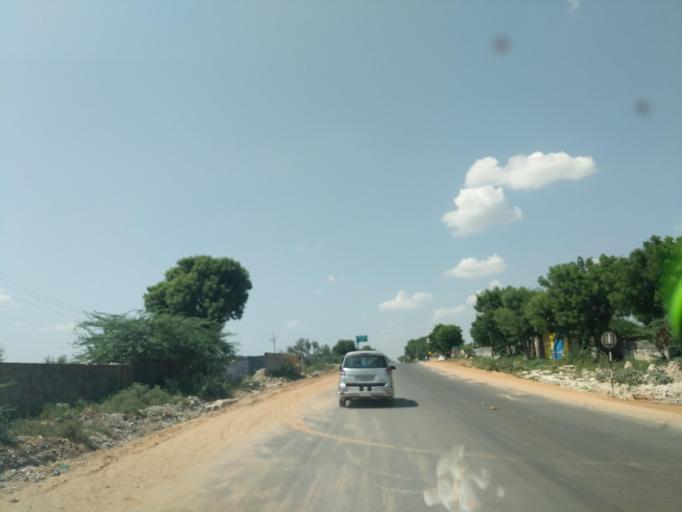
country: IN
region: Rajasthan
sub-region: Nagaur
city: Makrana
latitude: 27.0237
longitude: 74.7624
